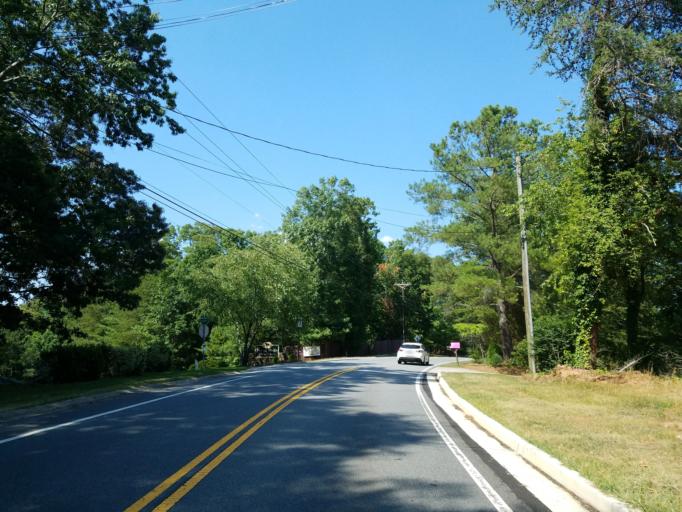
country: US
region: Georgia
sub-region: Fulton County
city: Roswell
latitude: 34.0442
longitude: -84.4352
